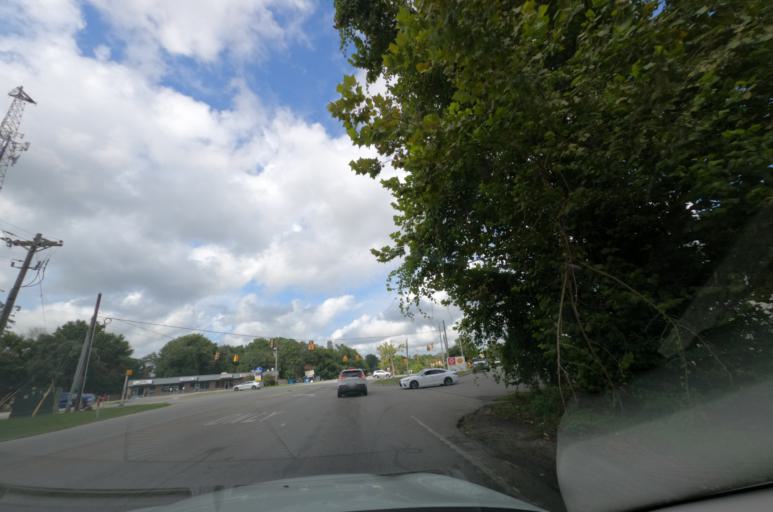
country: US
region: South Carolina
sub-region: Charleston County
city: Shell Point
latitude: 32.7203
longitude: -80.0824
